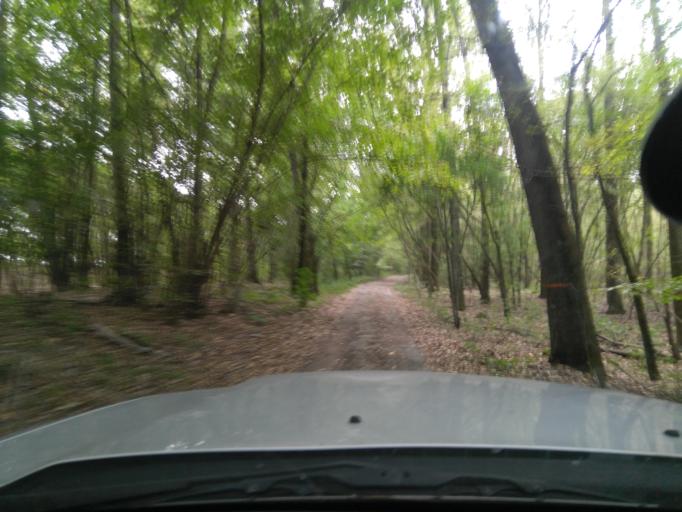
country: HU
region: Bacs-Kiskun
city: Apostag
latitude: 46.8962
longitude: 18.9481
